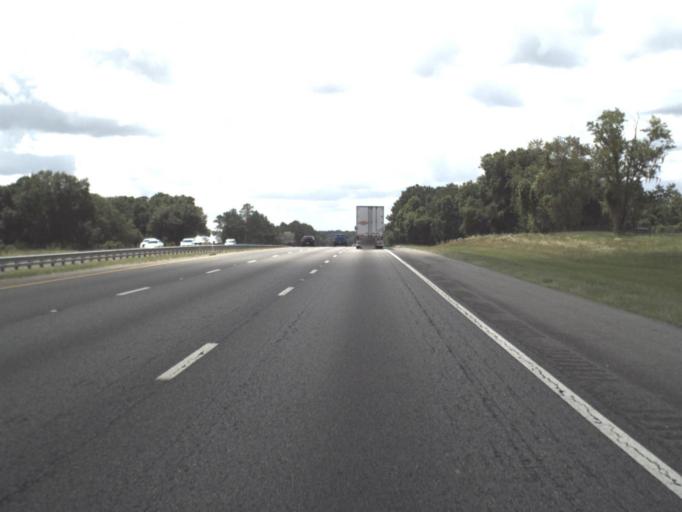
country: US
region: Florida
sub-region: Suwannee County
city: Wellborn
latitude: 30.2517
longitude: -82.7461
